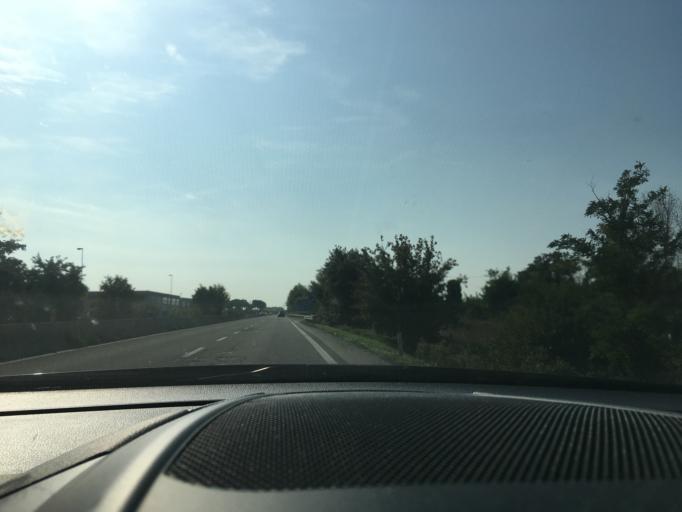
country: IT
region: Emilia-Romagna
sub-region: Provincia di Rimini
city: Bellaria-Igea Marina
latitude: 44.1315
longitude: 12.4660
